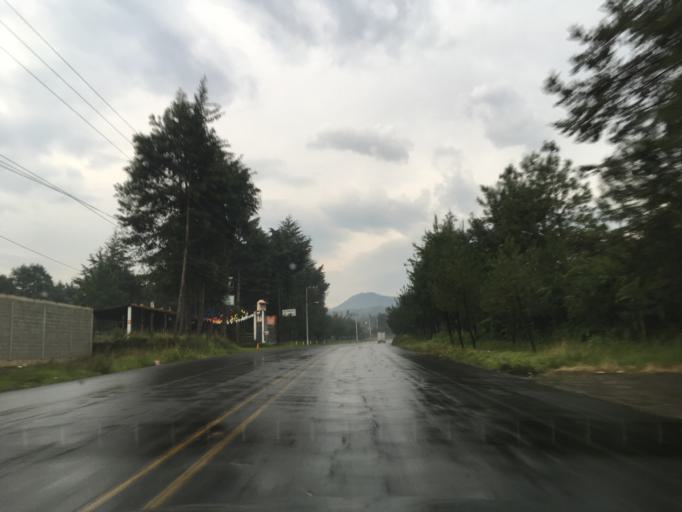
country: MX
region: Michoacan
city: Capacuaro
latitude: 19.5319
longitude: -102.0848
